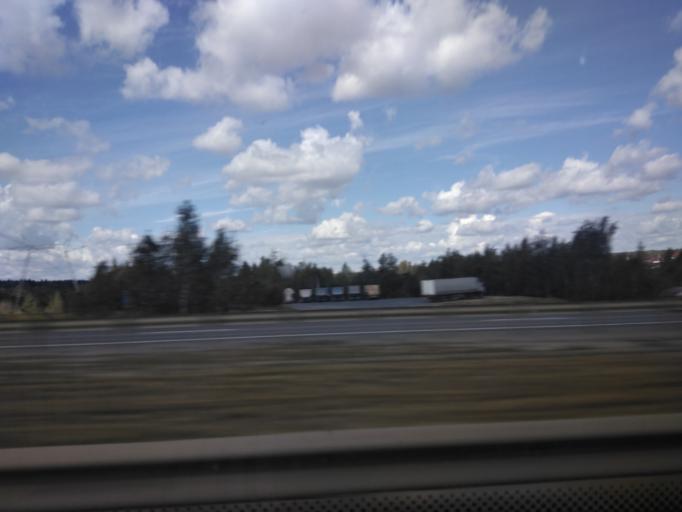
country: RU
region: Tula
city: Zaokskiy
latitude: 54.6904
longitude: 37.5084
